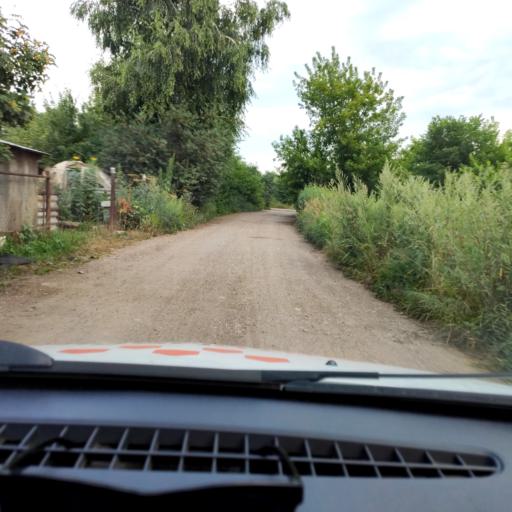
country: RU
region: Bashkortostan
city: Iglino
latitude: 54.7866
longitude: 56.1962
